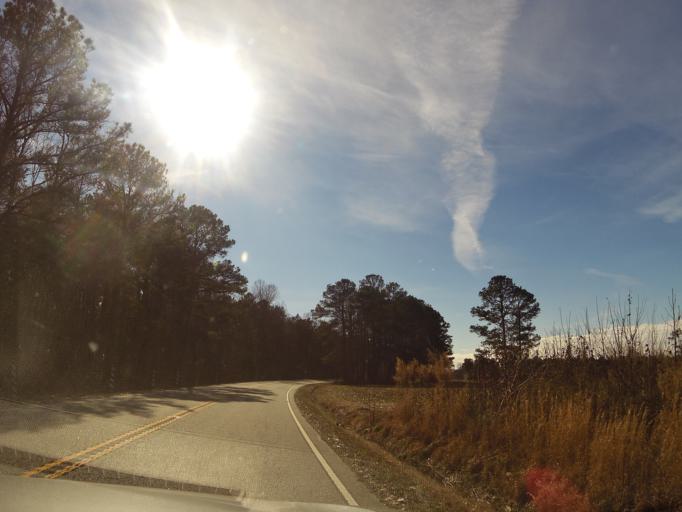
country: US
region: Virginia
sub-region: Isle of Wight County
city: Isle of Wight
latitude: 36.8744
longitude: -76.7294
